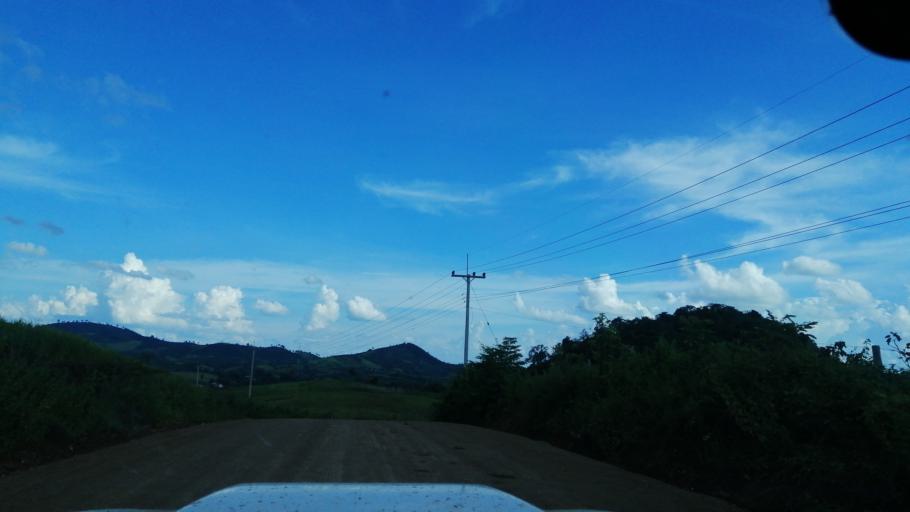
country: LA
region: Xiagnabouli
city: Muang Kenthao
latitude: 17.8548
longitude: 101.2365
